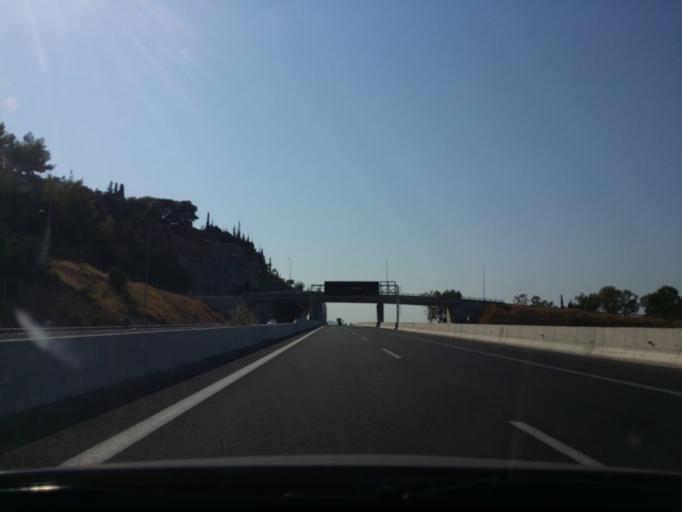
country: GR
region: Peloponnese
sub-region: Nomos Korinthias
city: Xylokastro
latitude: 38.0710
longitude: 22.6356
